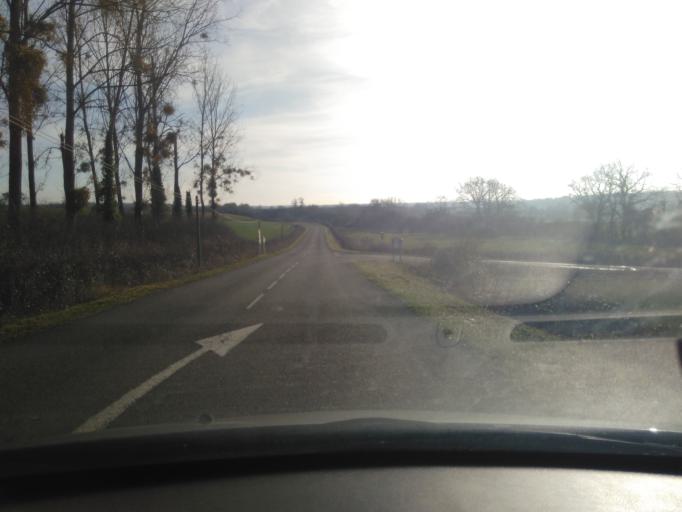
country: FR
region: Bourgogne
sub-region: Departement de la Nievre
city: Saint-Parize-le-Chatel
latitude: 46.8152
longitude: 3.2474
